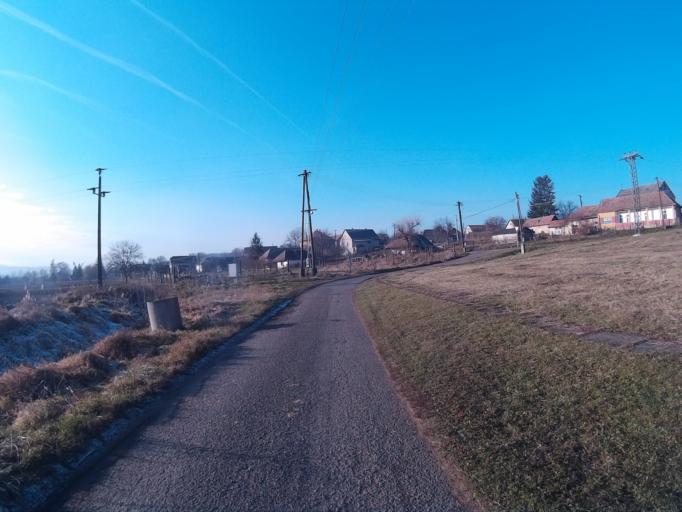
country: HU
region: Nograd
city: Bercel
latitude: 47.9763
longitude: 19.4311
